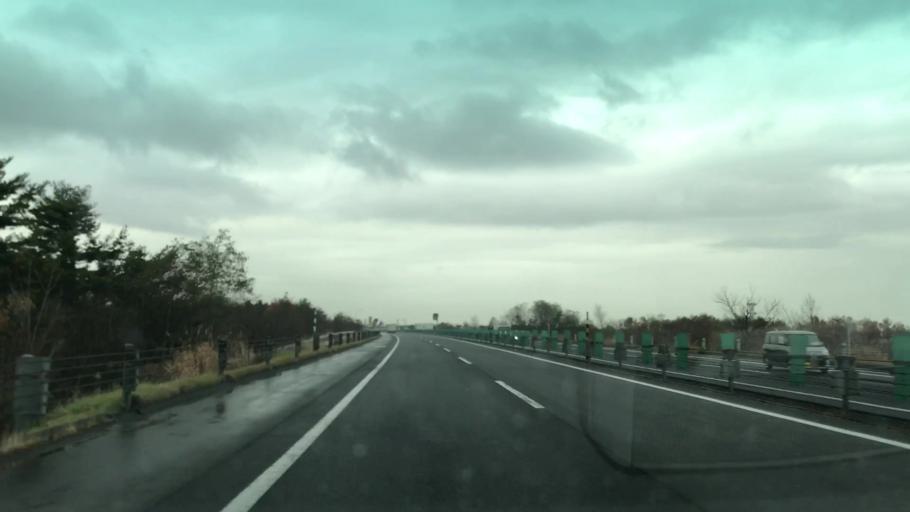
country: JP
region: Hokkaido
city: Kitahiroshima
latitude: 42.9037
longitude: 141.5506
